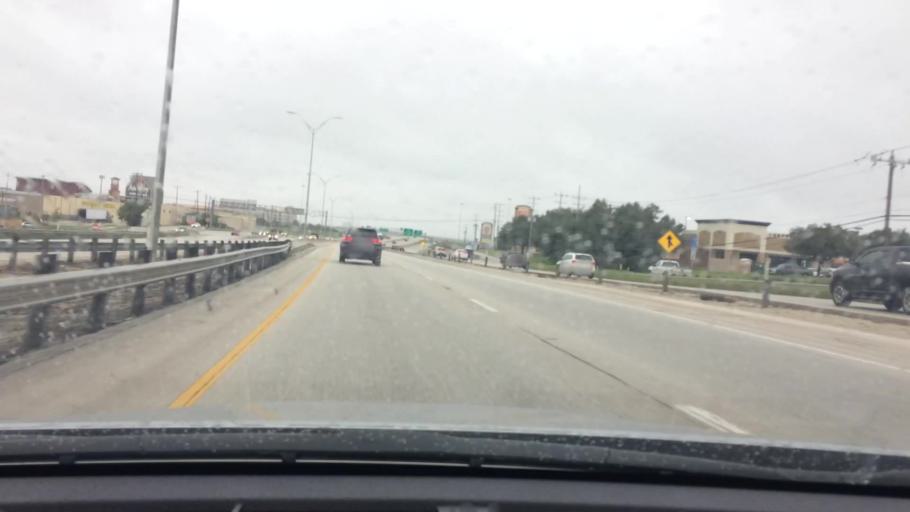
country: US
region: Texas
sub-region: Bexar County
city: Live Oak
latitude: 29.5624
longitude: -98.3284
